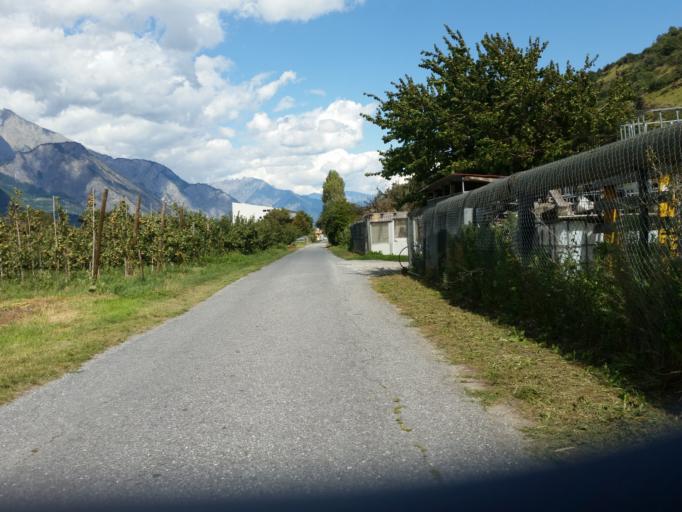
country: CH
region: Valais
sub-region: Martigny District
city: Charrat-les-Chenes
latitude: 46.1367
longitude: 7.1553
